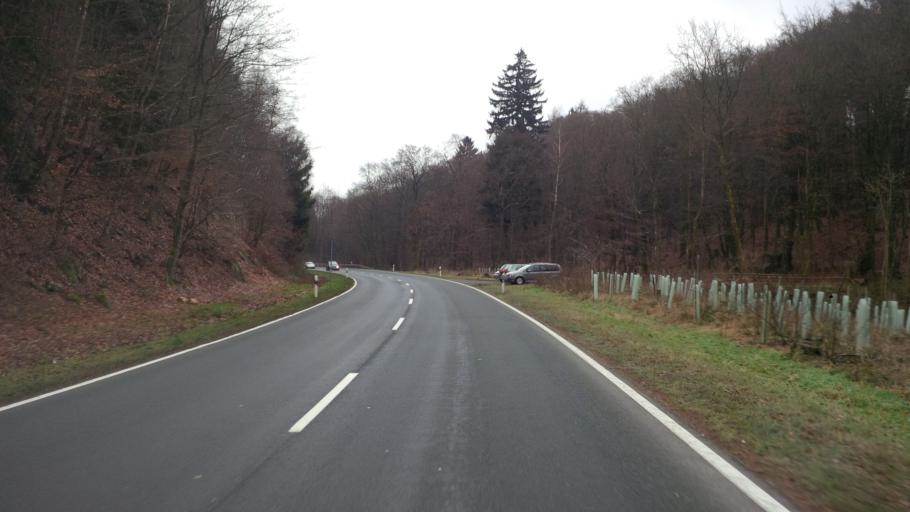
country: DE
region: Hesse
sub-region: Regierungsbezirk Darmstadt
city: Kronberg
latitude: 50.2216
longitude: 8.5202
